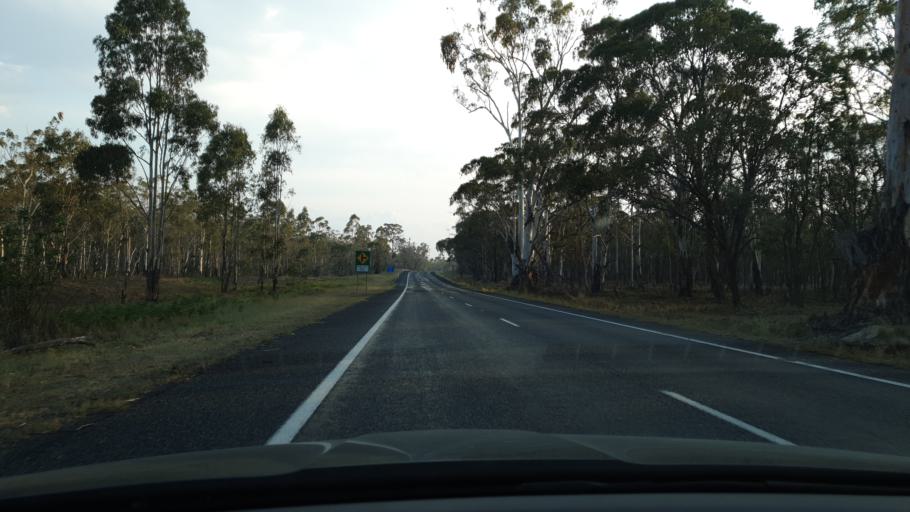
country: AU
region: New South Wales
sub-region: Tenterfield Municipality
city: Carrolls Creek
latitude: -29.2482
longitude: 151.9960
